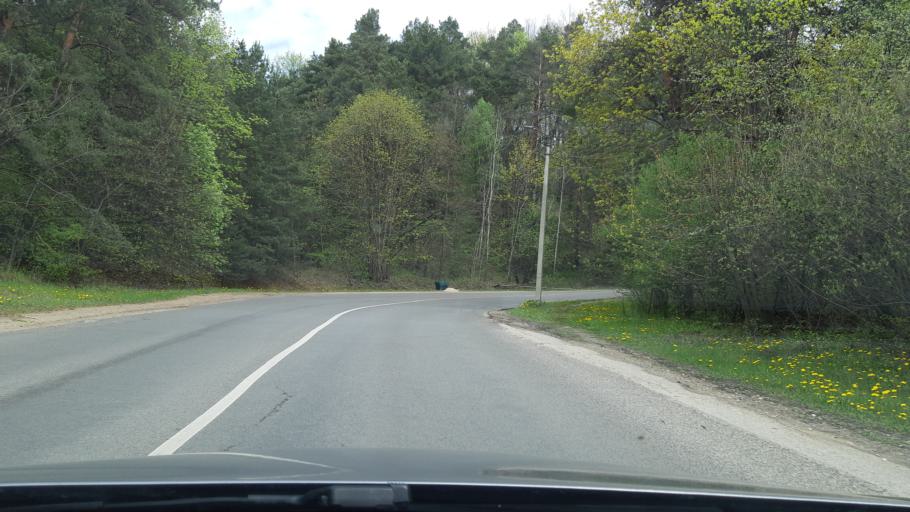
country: LT
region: Kauno apskritis
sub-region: Kauno rajonas
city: Akademija (Kaunas)
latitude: 54.9226
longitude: 23.8270
